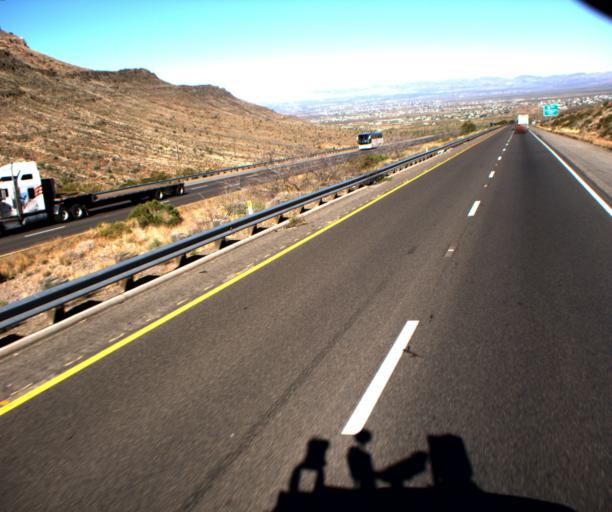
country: US
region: Arizona
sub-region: Mohave County
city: Kingman
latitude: 35.2107
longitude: -114.1076
